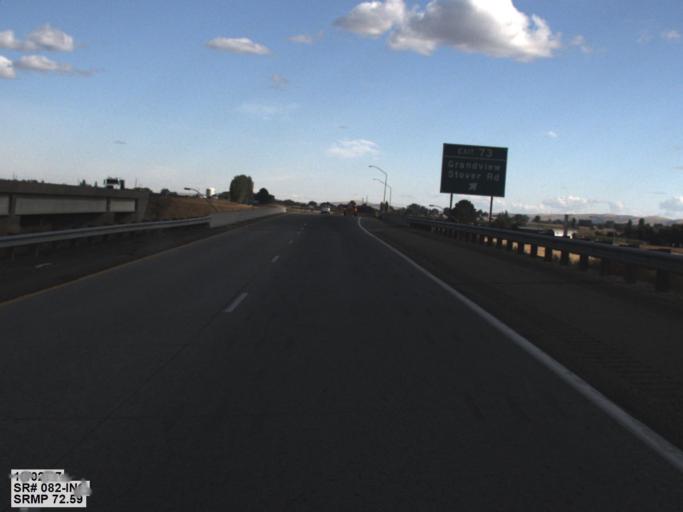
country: US
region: Washington
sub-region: Yakima County
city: Grandview
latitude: 46.2706
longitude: -119.9246
